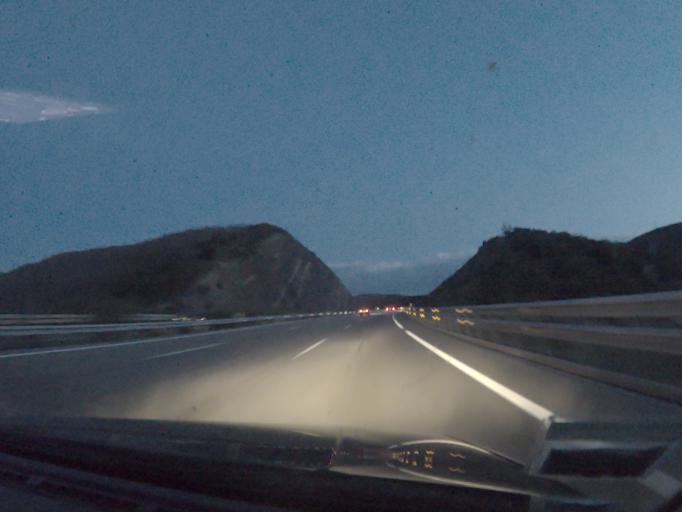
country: ES
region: Castille and Leon
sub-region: Provincia de Leon
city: Folgoso de la Ribera
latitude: 42.6181
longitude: -6.2789
